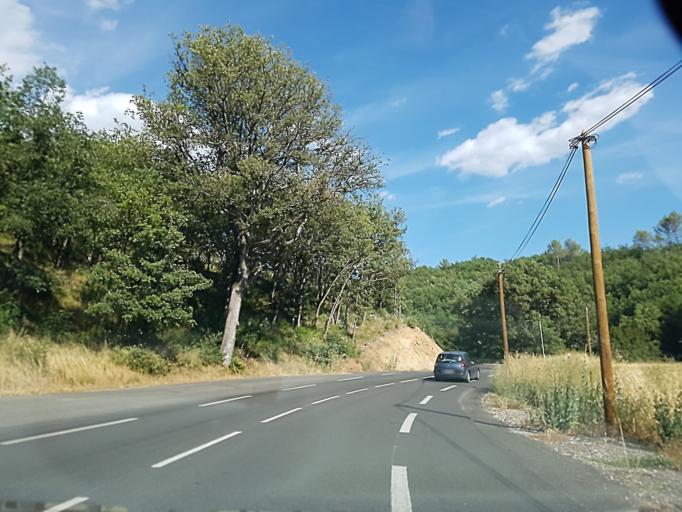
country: FR
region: Provence-Alpes-Cote d'Azur
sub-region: Departement du Var
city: Bras
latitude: 43.4602
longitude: 5.9297
